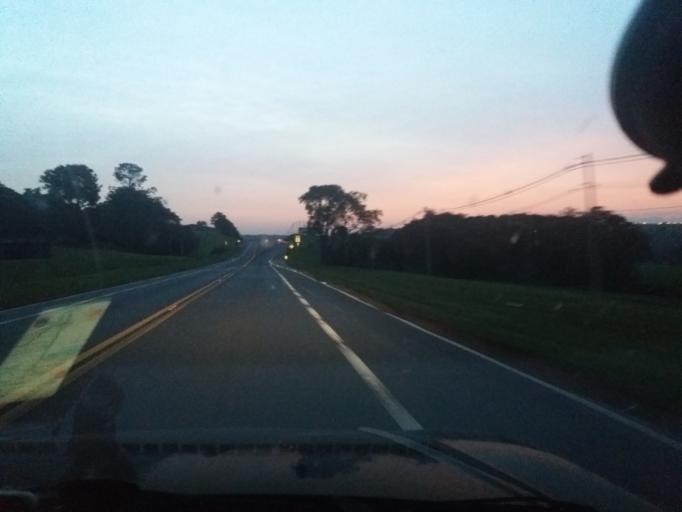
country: BR
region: Sao Paulo
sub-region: Itapeva
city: Itapeva
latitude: -23.9723
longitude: -48.8624
